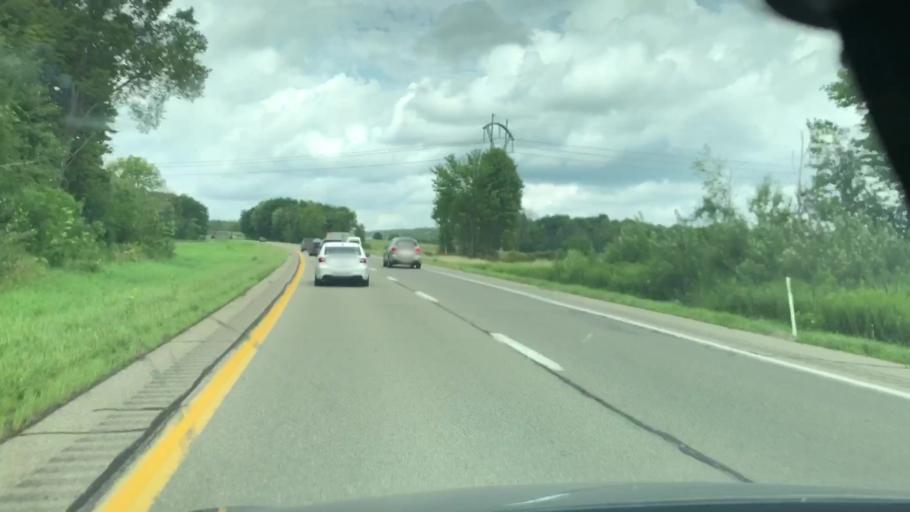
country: US
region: Pennsylvania
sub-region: Crawford County
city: Meadville
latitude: 41.7388
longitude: -80.1992
